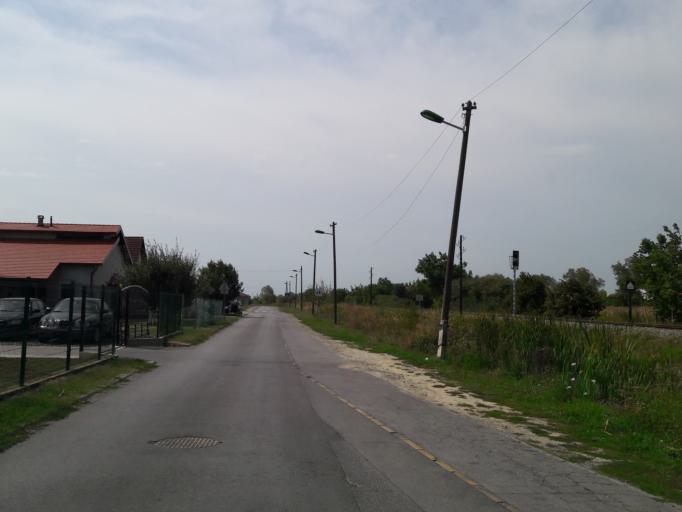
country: HR
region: Osjecko-Baranjska
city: Visnjevac
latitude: 45.5297
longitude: 18.6247
